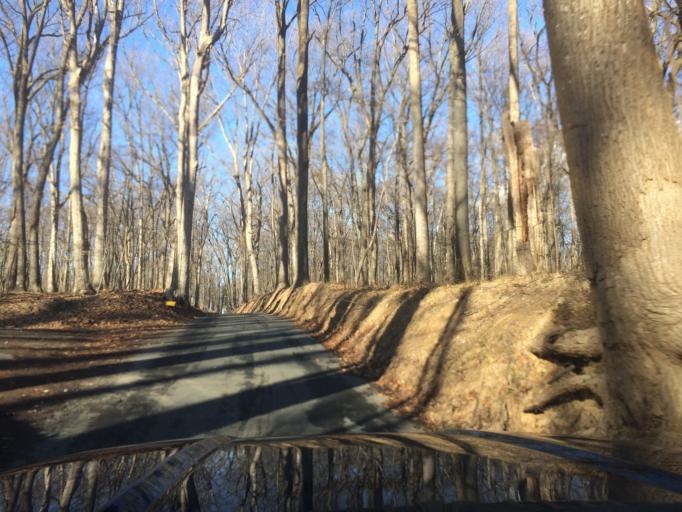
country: US
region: Maryland
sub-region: Carroll County
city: Eldersburg
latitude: 39.3600
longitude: -76.8956
